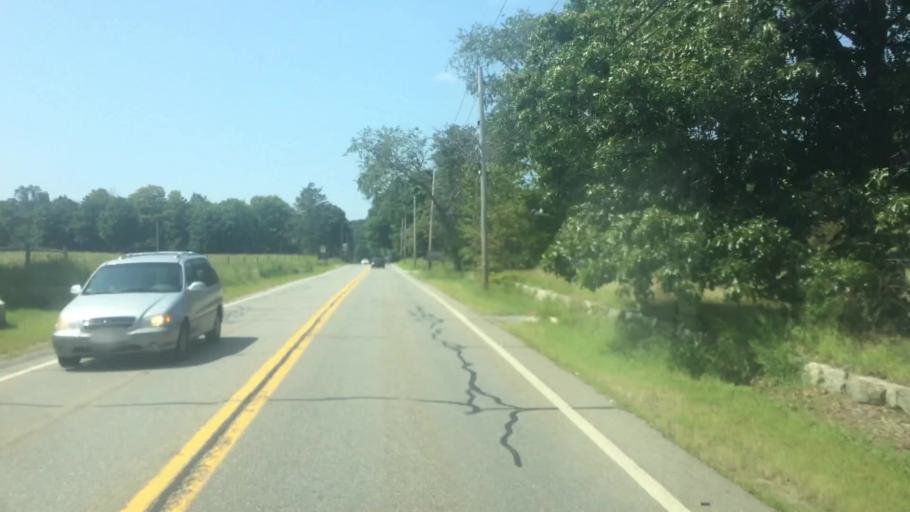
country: US
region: Massachusetts
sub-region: Middlesex County
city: Lincoln
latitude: 42.4530
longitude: -71.3068
